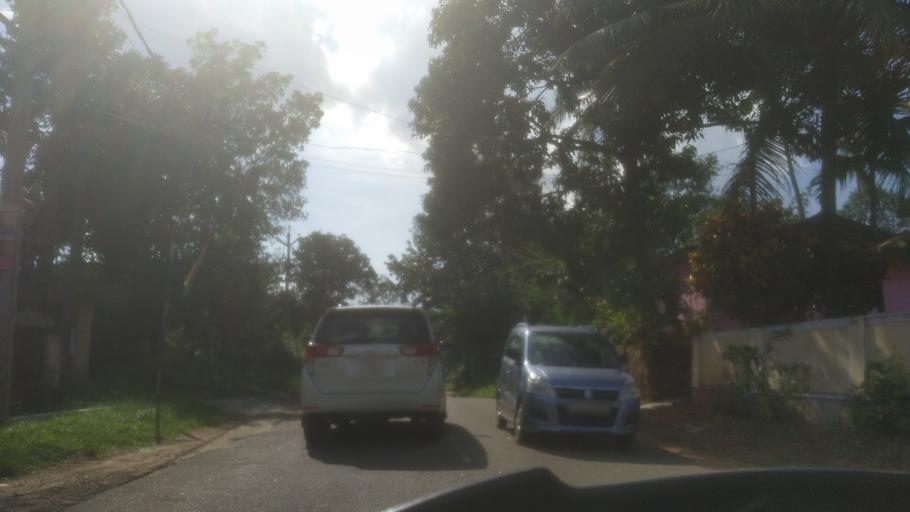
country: IN
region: Kerala
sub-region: Ernakulam
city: Muvattupula
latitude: 9.9976
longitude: 76.6169
